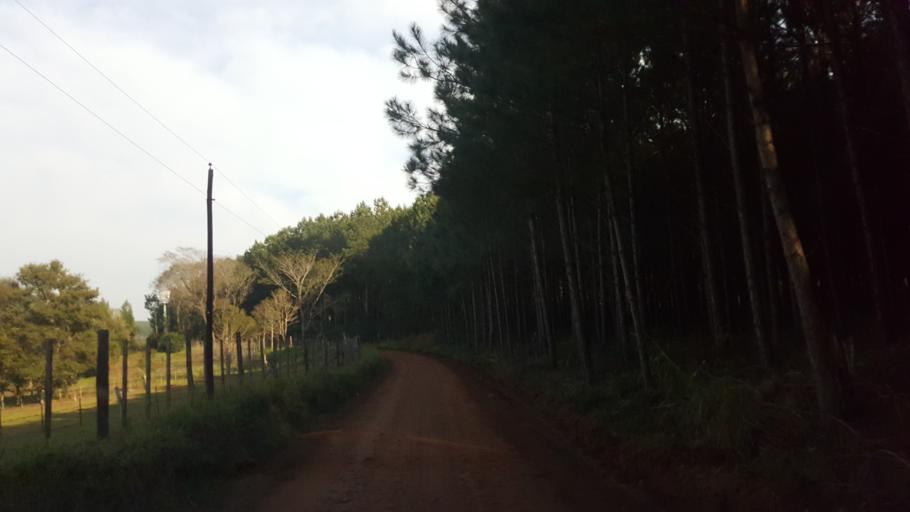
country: AR
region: Misiones
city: Capiovi
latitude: -26.9150
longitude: -55.0732
